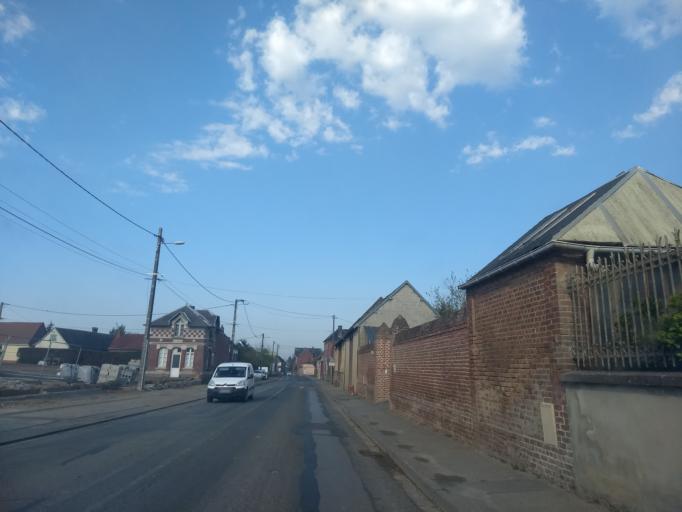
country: FR
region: Picardie
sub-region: Departement de la Somme
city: Corbie
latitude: 50.0117
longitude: 2.5230
